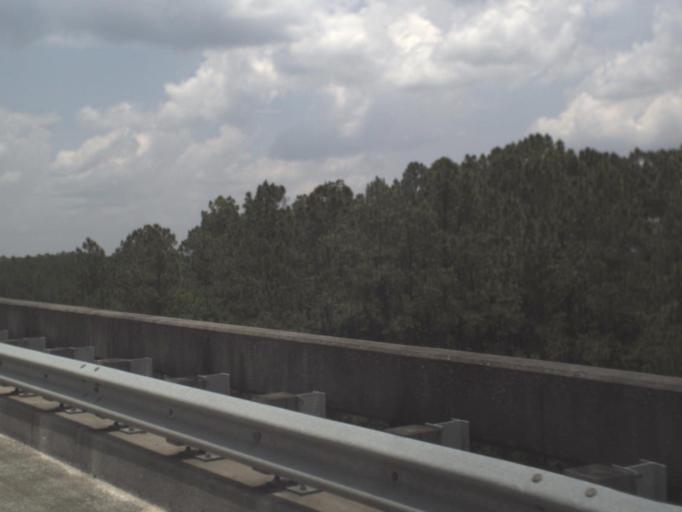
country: US
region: Florida
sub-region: Putnam County
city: Interlachen
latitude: 29.5324
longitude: -81.7557
